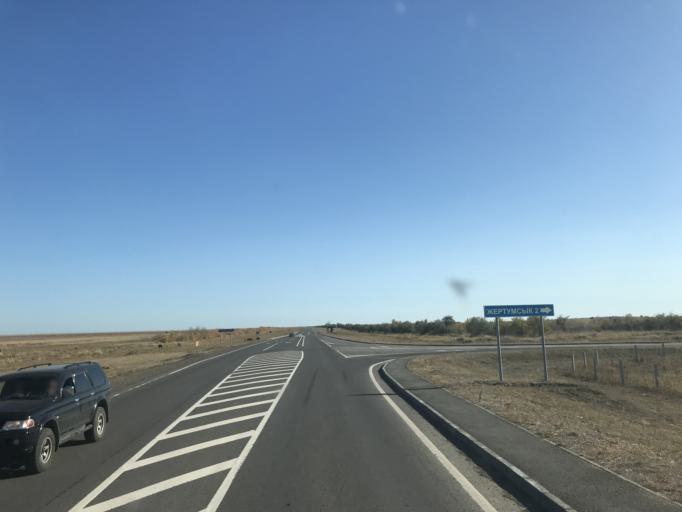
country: KZ
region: Pavlodar
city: Aksu
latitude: 52.0638
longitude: 77.1635
